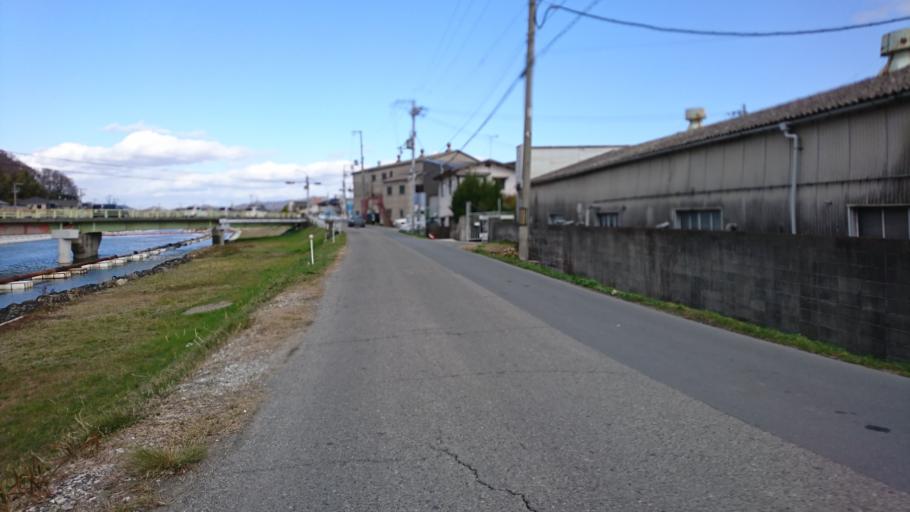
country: JP
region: Hyogo
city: Kakogawacho-honmachi
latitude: 34.7734
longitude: 134.7986
